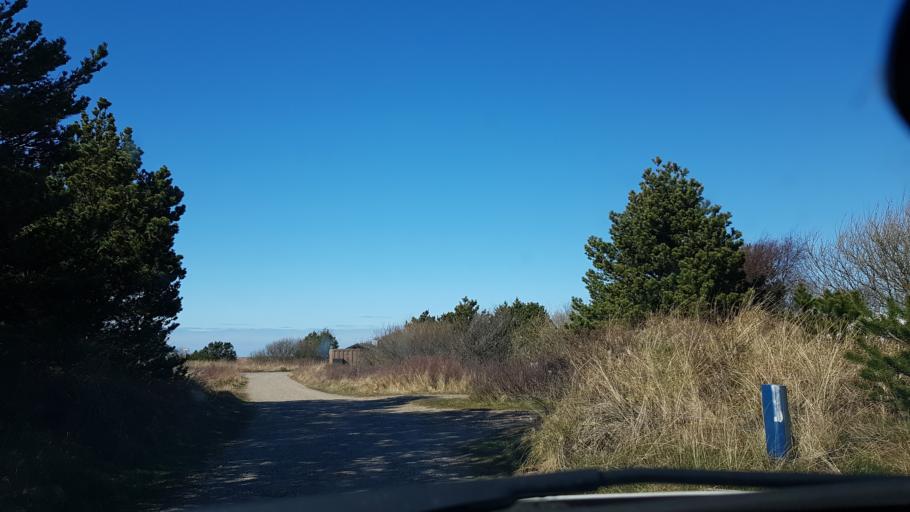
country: DE
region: Schleswig-Holstein
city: List
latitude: 55.1557
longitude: 8.5168
